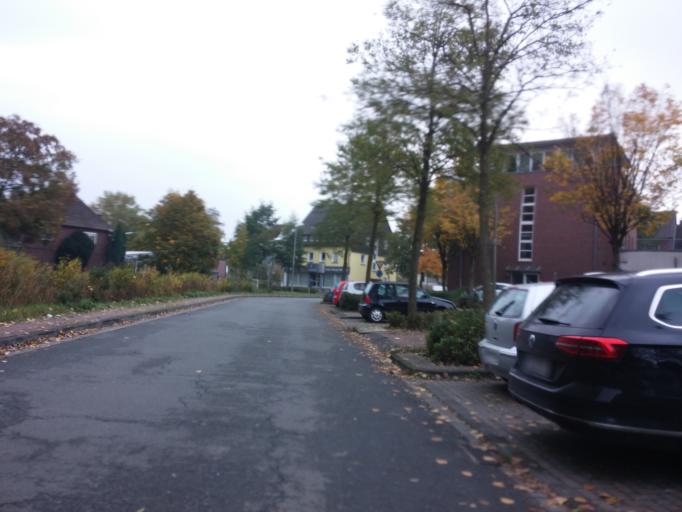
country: DE
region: North Rhine-Westphalia
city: Dorsten
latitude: 51.6611
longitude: 6.9468
